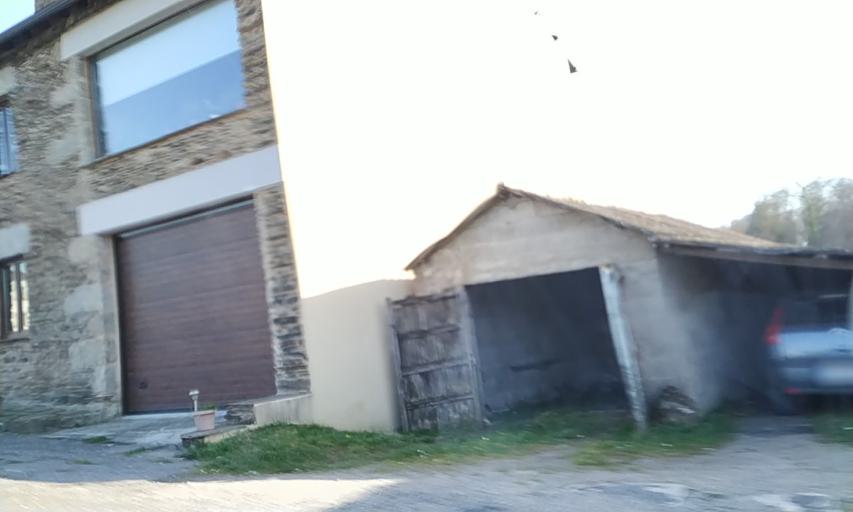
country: ES
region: Galicia
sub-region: Provincia de Lugo
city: Corgo
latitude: 42.9587
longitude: -7.4738
